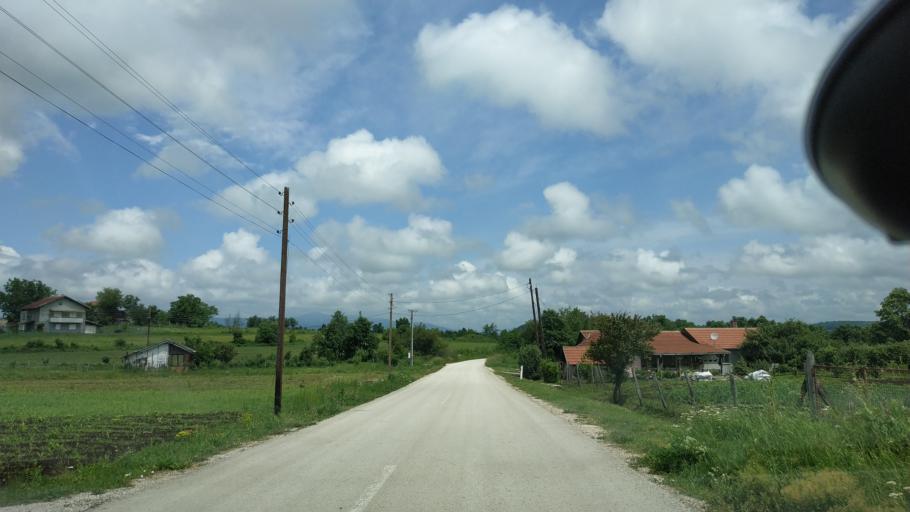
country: RS
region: Central Serbia
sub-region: Zajecarski Okrug
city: Boljevac
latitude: 43.8171
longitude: 21.9518
